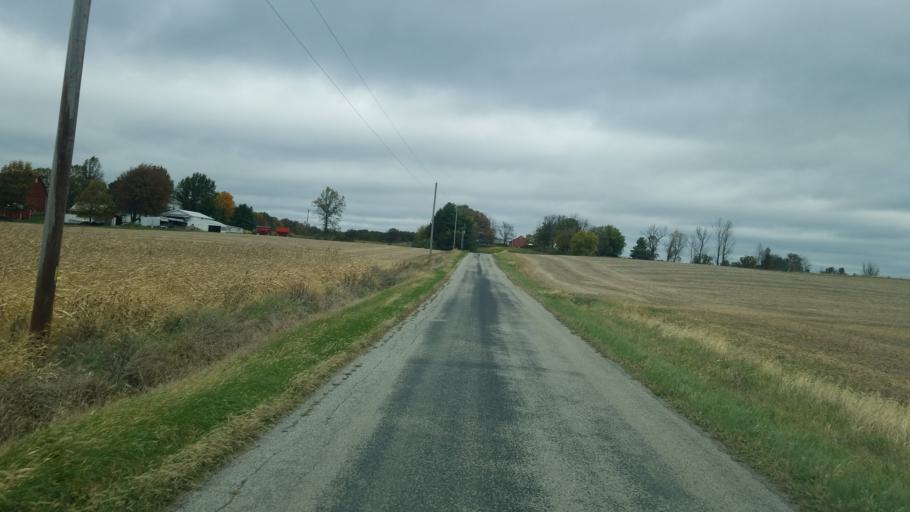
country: US
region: Ohio
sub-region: Huron County
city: Willard
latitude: 40.9432
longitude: -82.8117
